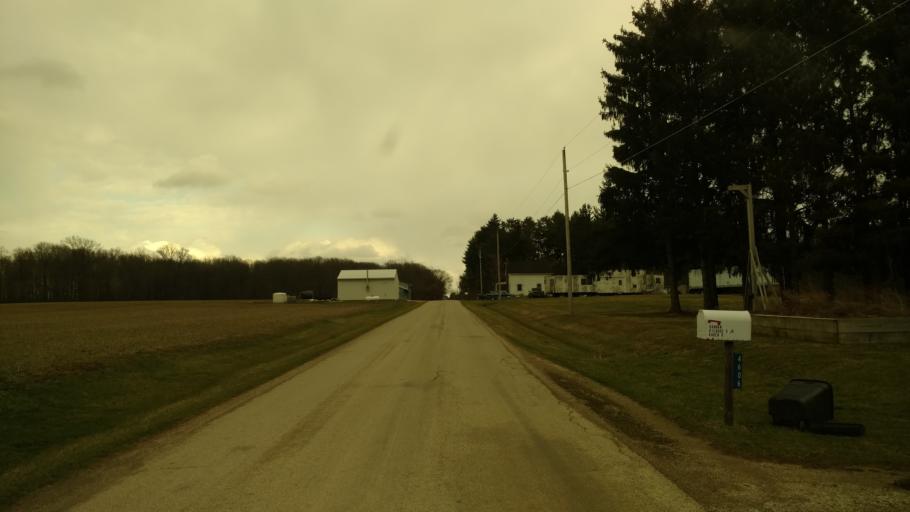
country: US
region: Ohio
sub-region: Crawford County
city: Galion
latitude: 40.6686
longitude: -82.7937
